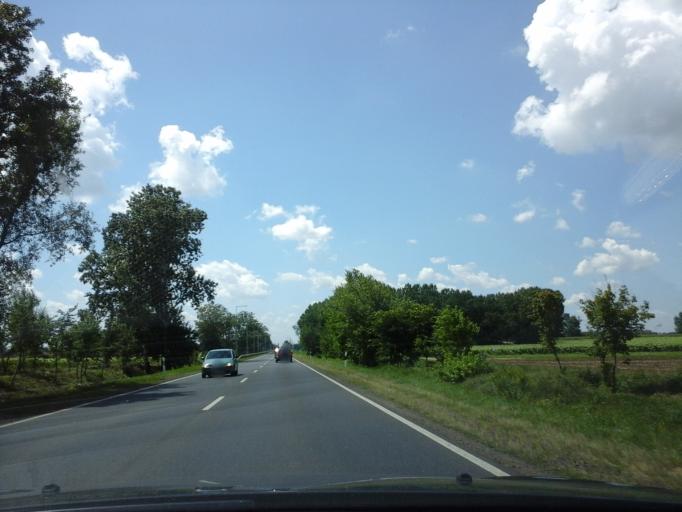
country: HU
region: Hajdu-Bihar
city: Ebes
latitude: 47.4795
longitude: 21.4941
